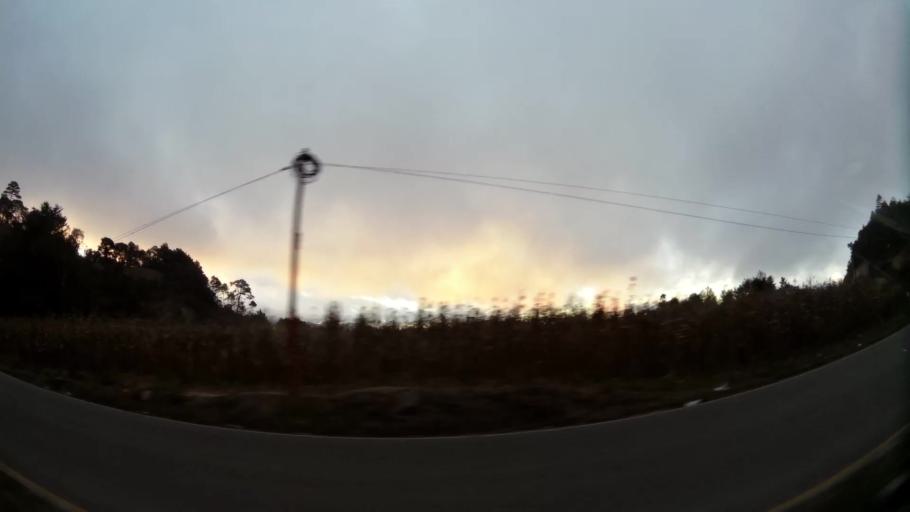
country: GT
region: Solola
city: Concepcion
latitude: 14.8461
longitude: -91.1403
